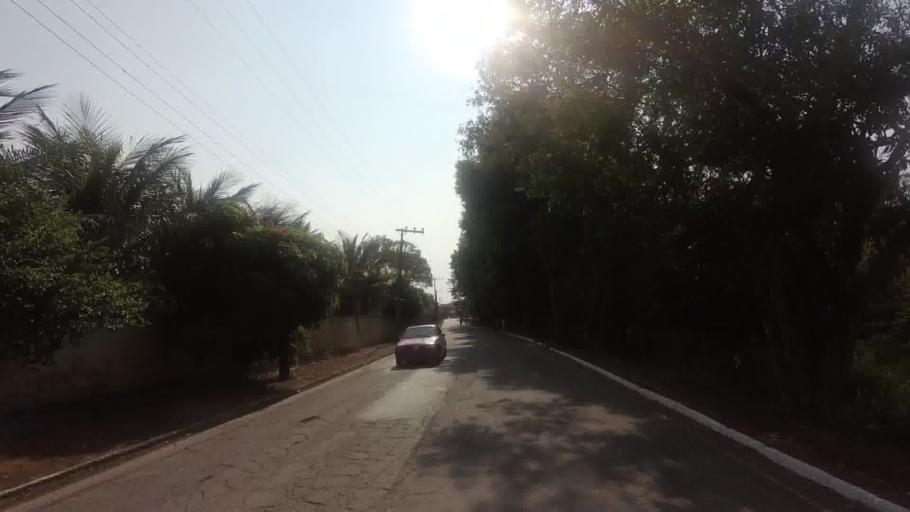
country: BR
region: Rio de Janeiro
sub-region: Bom Jesus Do Itabapoana
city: Bom Jesus do Itabapoana
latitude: -21.1462
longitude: -41.6217
